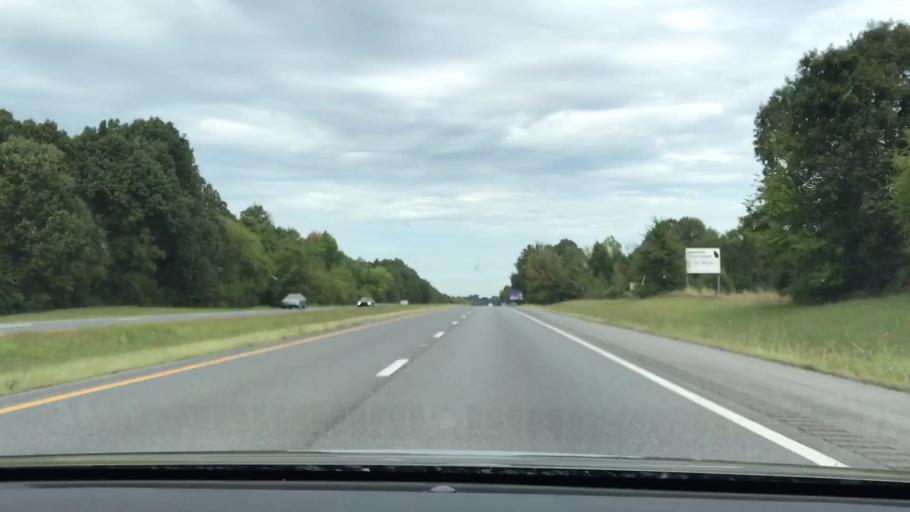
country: US
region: Kentucky
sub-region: Marshall County
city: Benton
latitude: 36.9063
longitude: -88.3482
